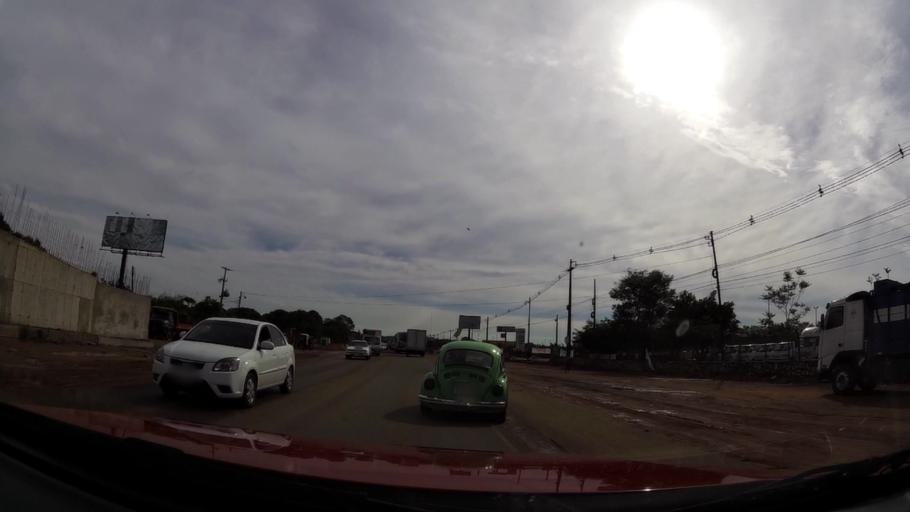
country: PY
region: Central
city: Limpio
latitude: -25.1767
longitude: -57.4855
